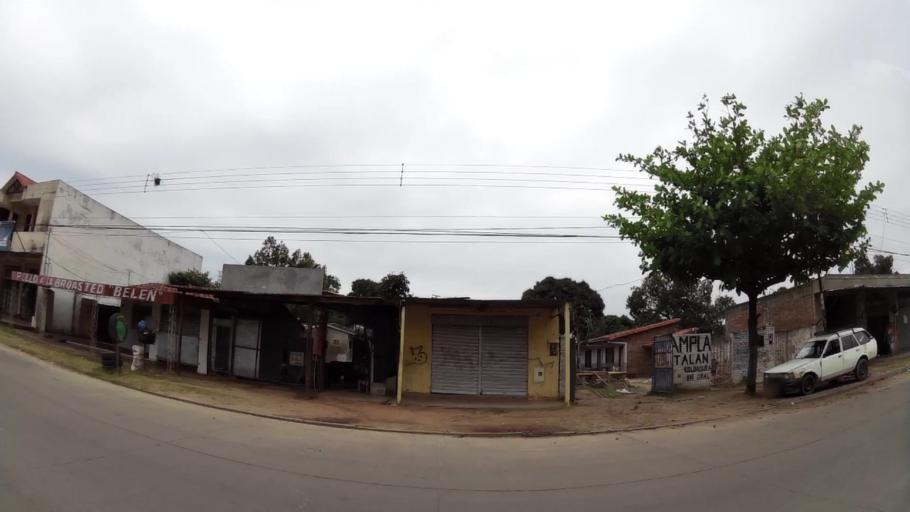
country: BO
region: Santa Cruz
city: Santa Cruz de la Sierra
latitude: -17.8316
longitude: -63.1797
